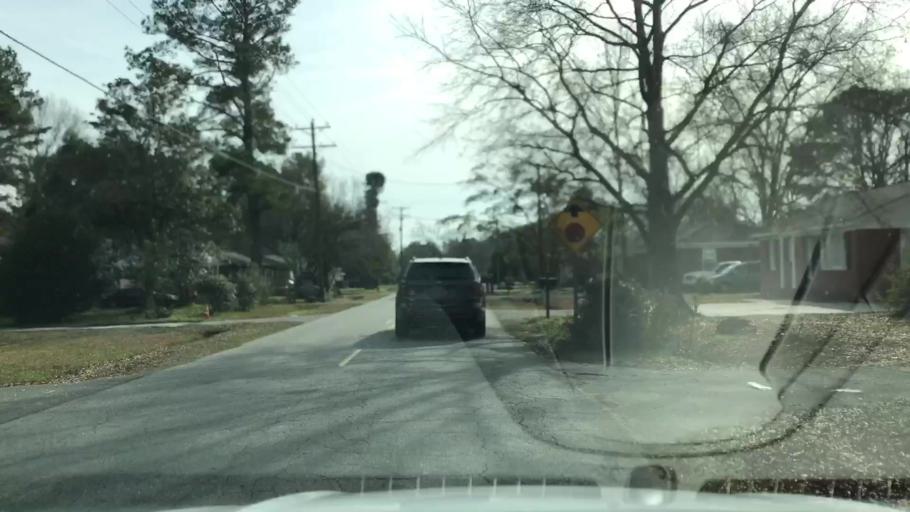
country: US
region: South Carolina
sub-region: Berkeley County
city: Goose Creek
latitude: 33.0190
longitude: -80.0290
